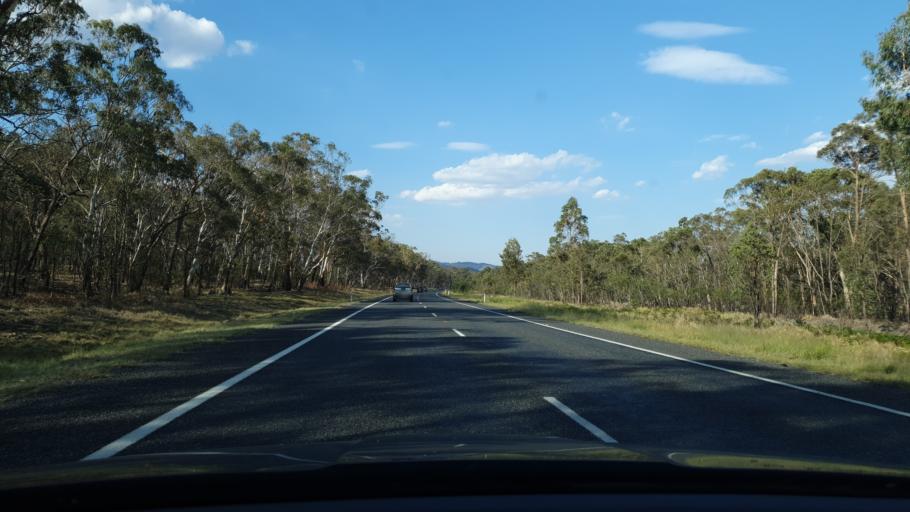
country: AU
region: New South Wales
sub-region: Tenterfield Municipality
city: Carrolls Creek
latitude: -29.2419
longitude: 151.9985
